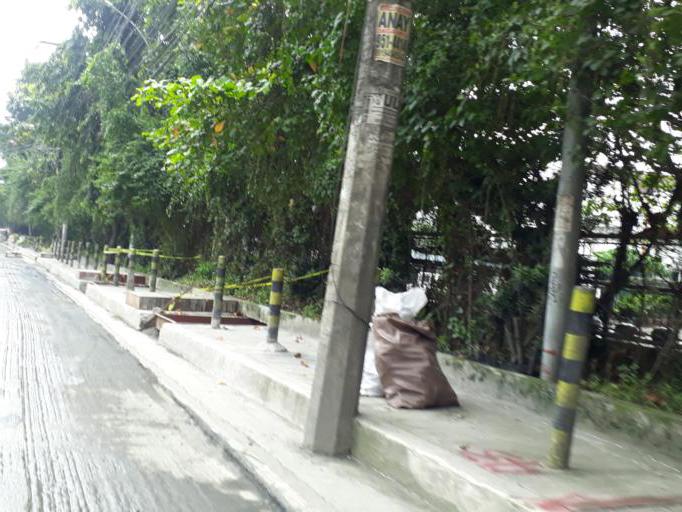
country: PH
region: Calabarzon
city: Bagong Pagasa
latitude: 14.6797
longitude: 121.0216
